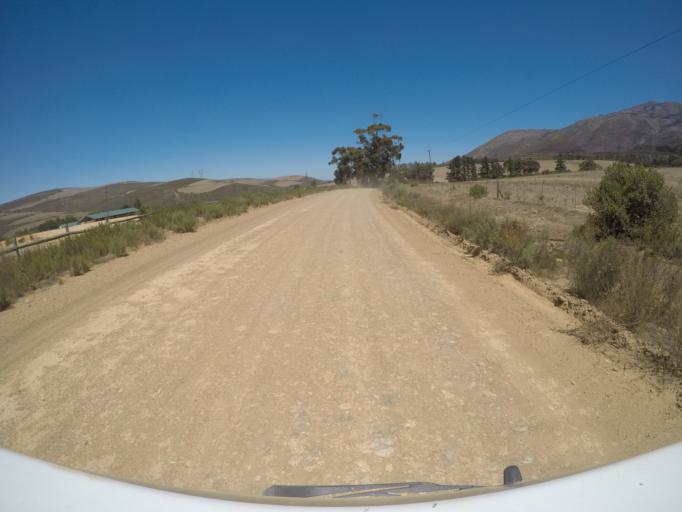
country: ZA
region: Western Cape
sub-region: Overberg District Municipality
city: Caledon
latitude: -34.1932
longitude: 19.2250
